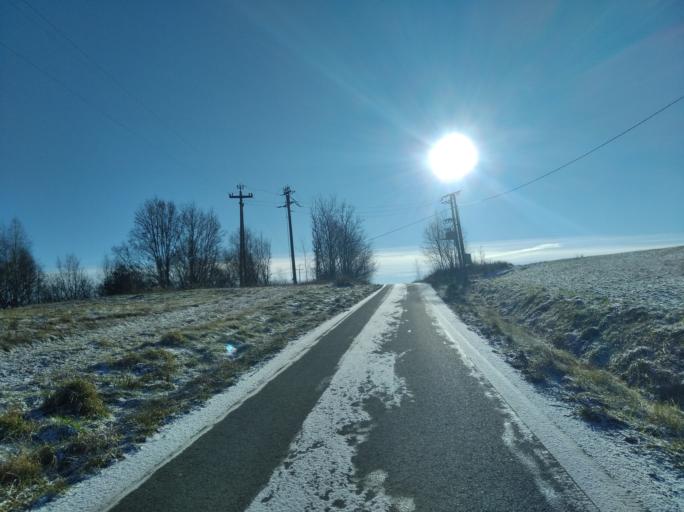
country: PL
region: Subcarpathian Voivodeship
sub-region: Powiat strzyzowski
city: Czudec
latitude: 49.9432
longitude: 21.7668
